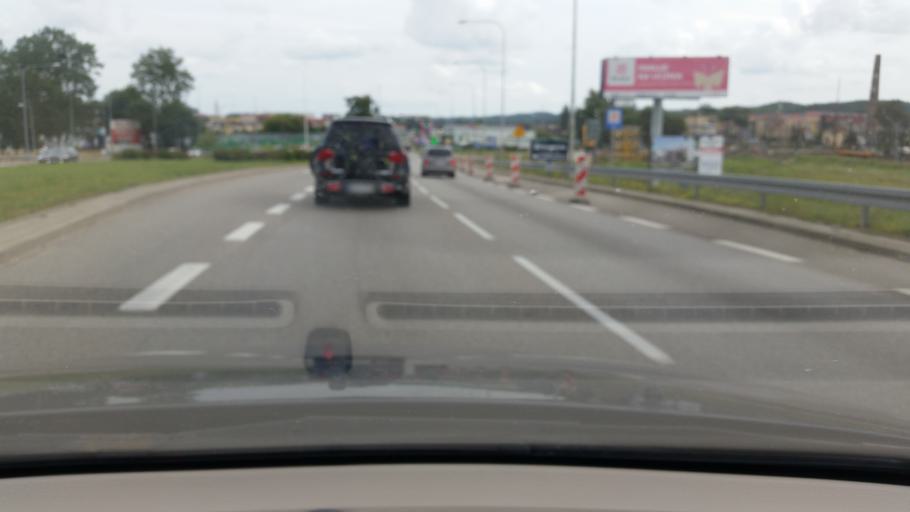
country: PL
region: Pomeranian Voivodeship
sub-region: Powiat wejherowski
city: Wejherowo
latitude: 54.6079
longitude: 18.2206
